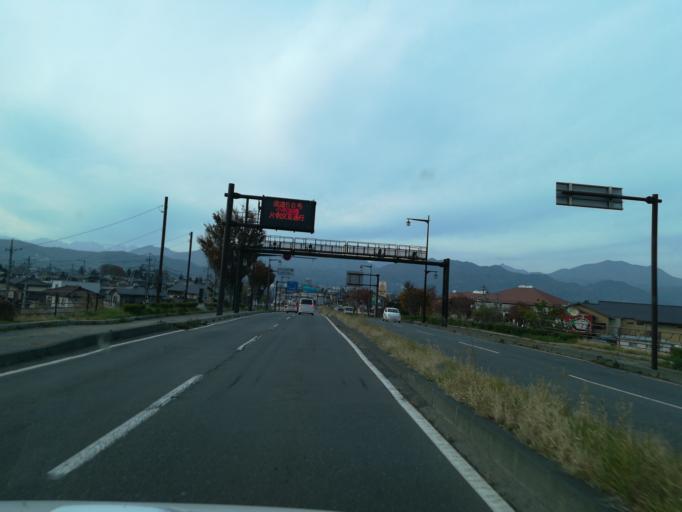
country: JP
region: Nagano
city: Nagano-shi
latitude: 36.5830
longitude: 138.1910
